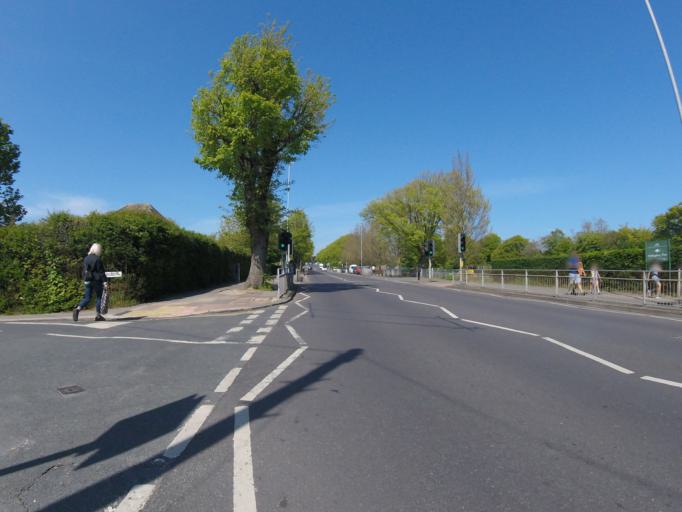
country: GB
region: England
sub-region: Brighton and Hove
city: Brighton
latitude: 50.8489
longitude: -0.1353
